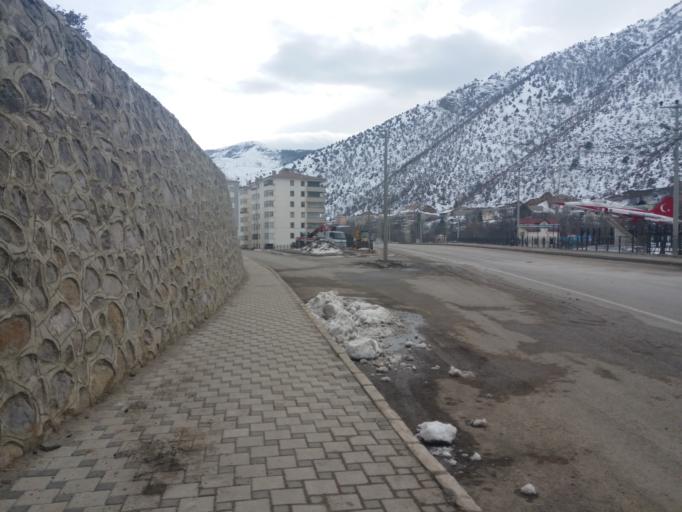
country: TR
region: Gumushane
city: Gumushkhane
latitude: 40.4402
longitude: 39.5039
